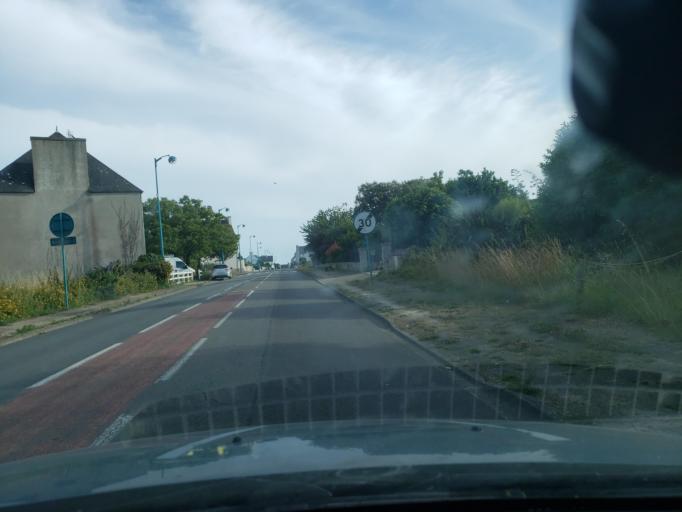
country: FR
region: Brittany
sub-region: Departement du Finistere
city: Treffiagat
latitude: 47.8039
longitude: -4.2634
